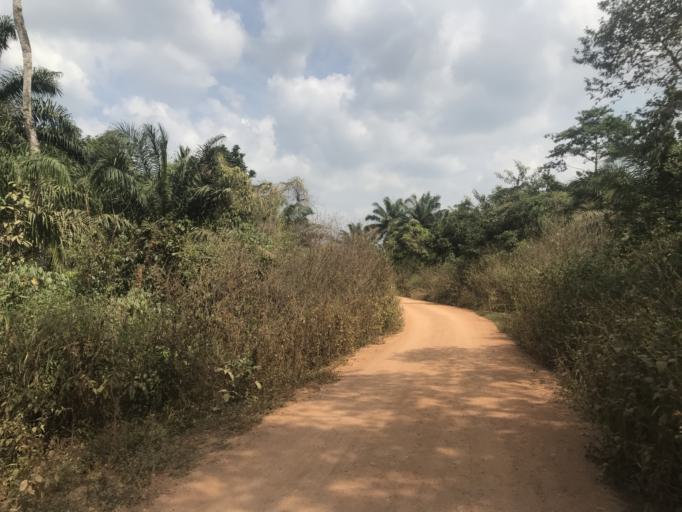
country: NG
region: Osun
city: Inisa
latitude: 7.8759
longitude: 4.3840
